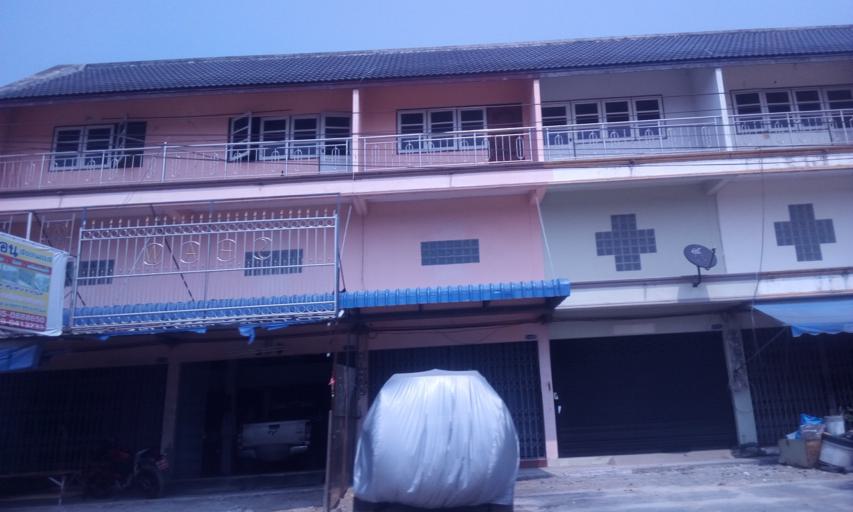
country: TH
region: Chon Buri
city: Phanat Nikhom
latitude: 13.4303
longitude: 101.1826
